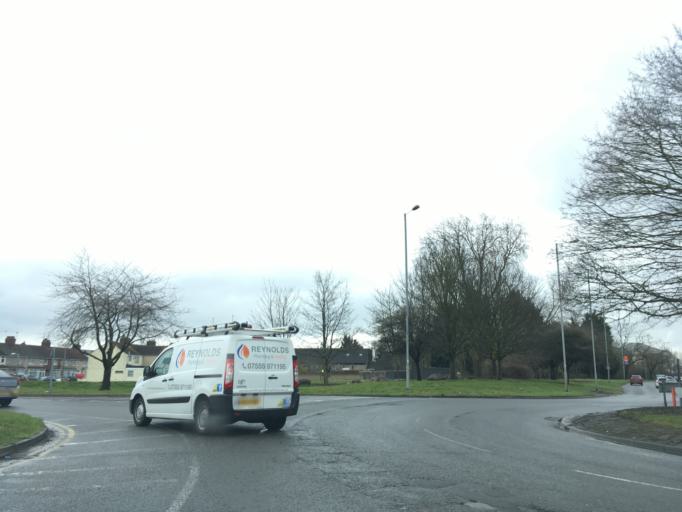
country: GB
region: England
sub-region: Borough of Swindon
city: Swindon
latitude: 51.5700
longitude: -1.7890
